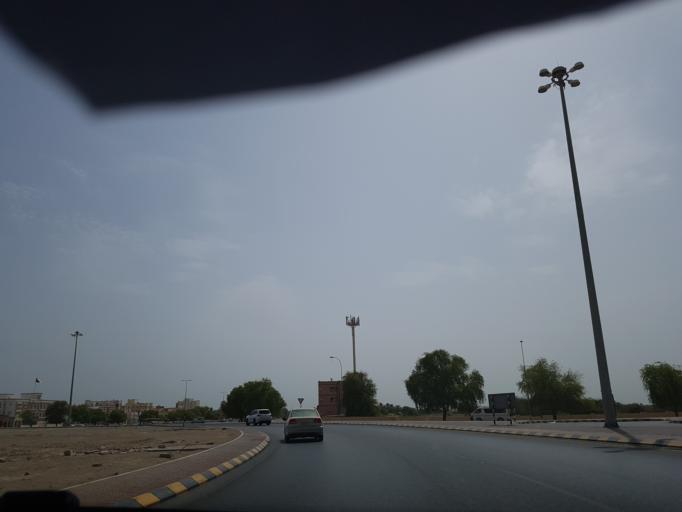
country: OM
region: Al Batinah
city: As Suwayq
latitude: 23.7541
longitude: 57.5764
